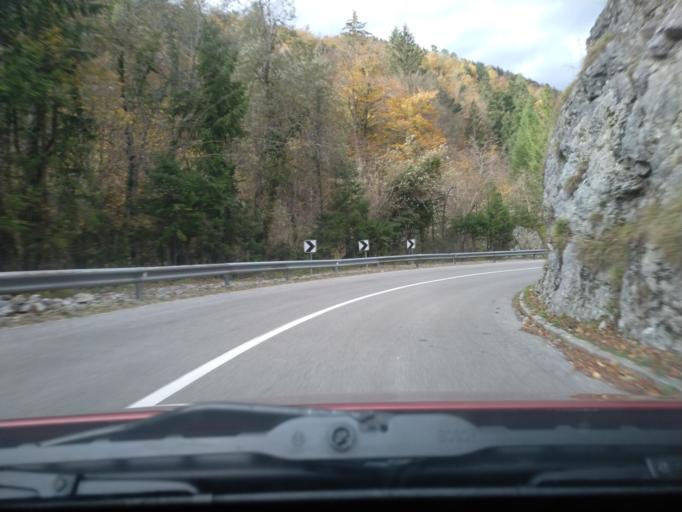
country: SI
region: Kamnik
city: Mekinje
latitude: 46.2798
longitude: 14.6144
